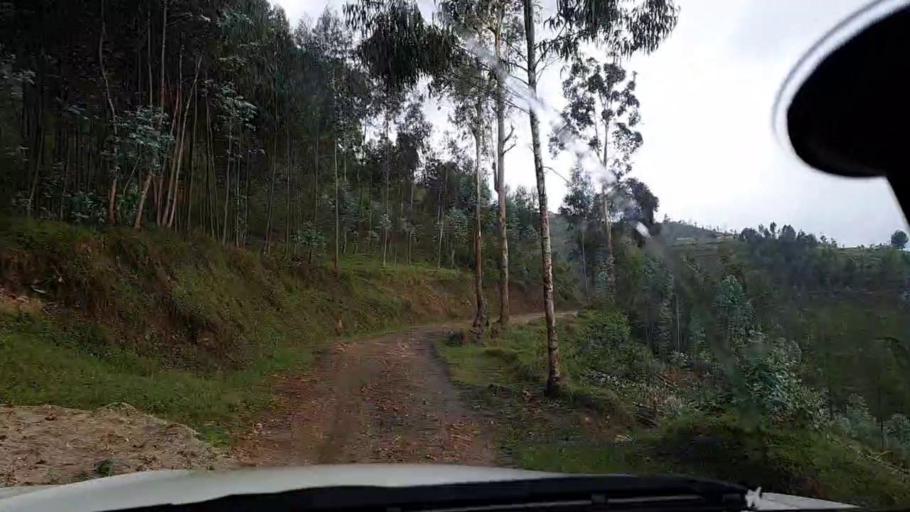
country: RW
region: Western Province
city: Kibuye
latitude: -2.0775
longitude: 29.5141
